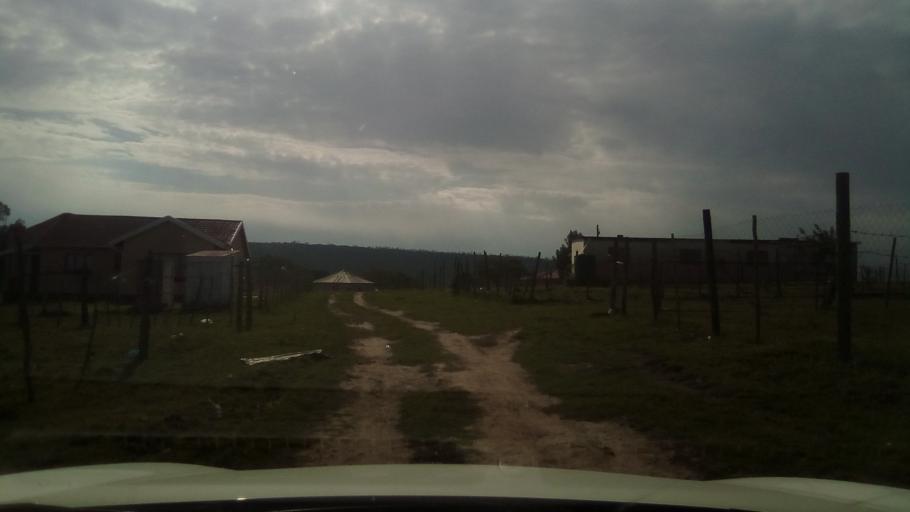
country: ZA
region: Eastern Cape
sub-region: Buffalo City Metropolitan Municipality
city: Bhisho
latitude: -32.9868
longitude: 27.2658
